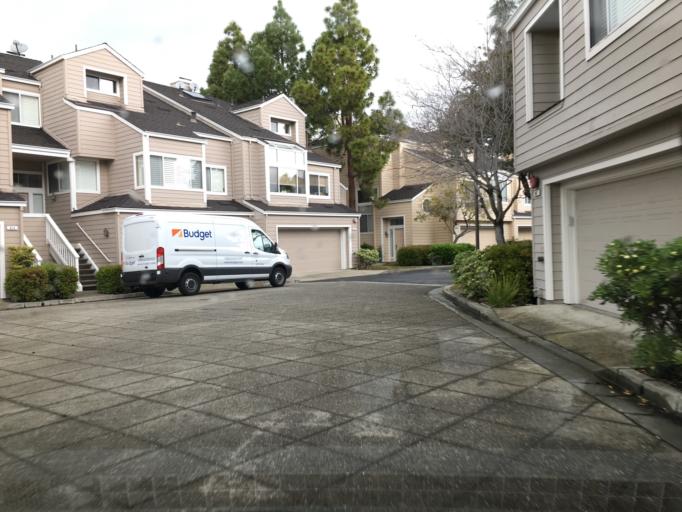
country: US
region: California
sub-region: San Mateo County
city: Redwood Shores
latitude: 37.5370
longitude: -122.2394
